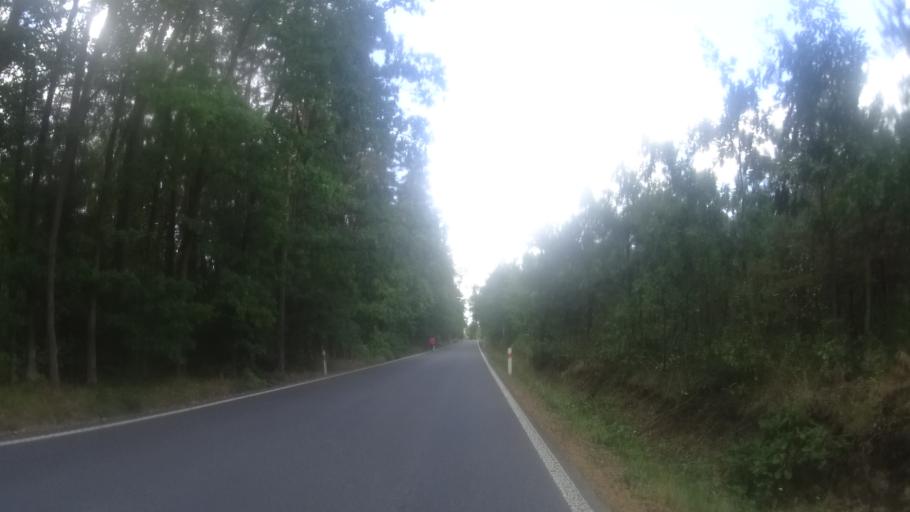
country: CZ
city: Borohradek
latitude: 50.0815
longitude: 16.1185
